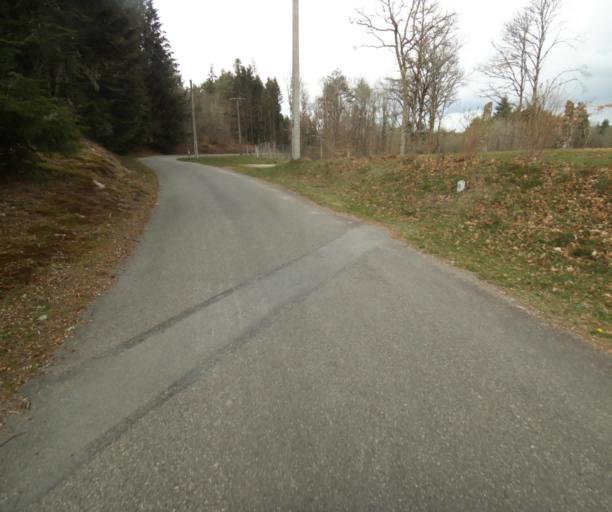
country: FR
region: Limousin
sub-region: Departement de la Correze
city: Correze
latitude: 45.2853
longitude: 1.9698
